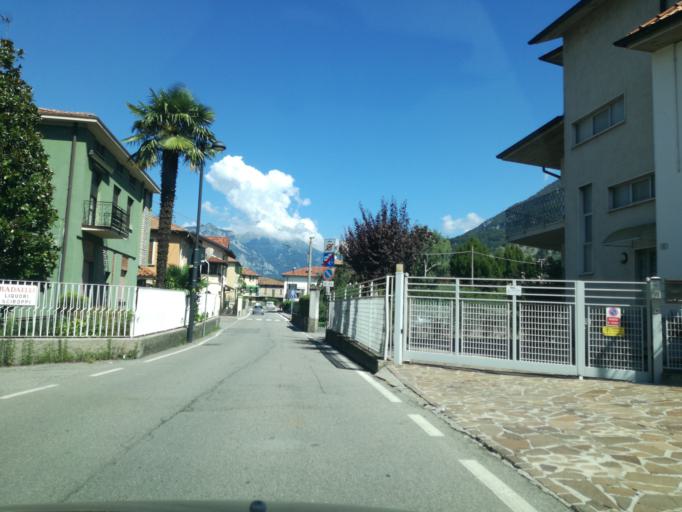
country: IT
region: Lombardy
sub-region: Provincia di Lecco
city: Vercurago
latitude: 45.8047
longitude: 9.4198
